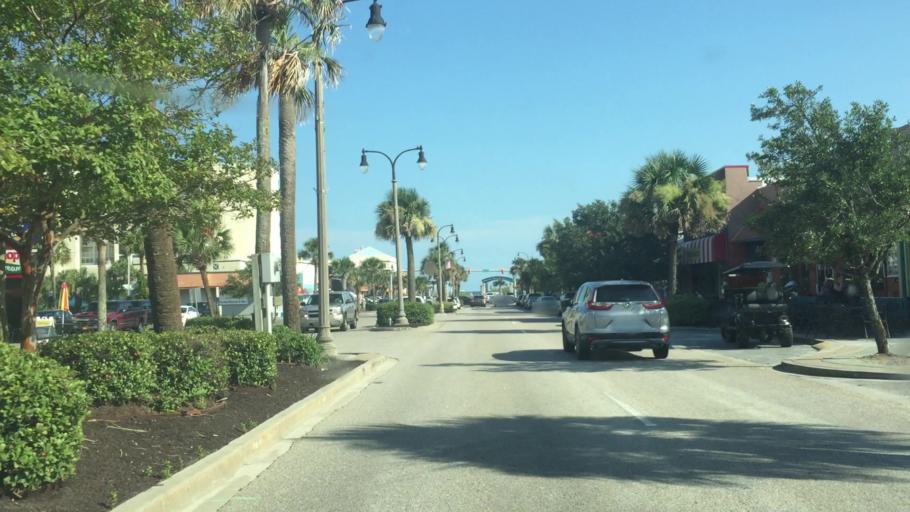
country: US
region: South Carolina
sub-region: Horry County
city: North Myrtle Beach
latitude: 33.8200
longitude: -78.6731
